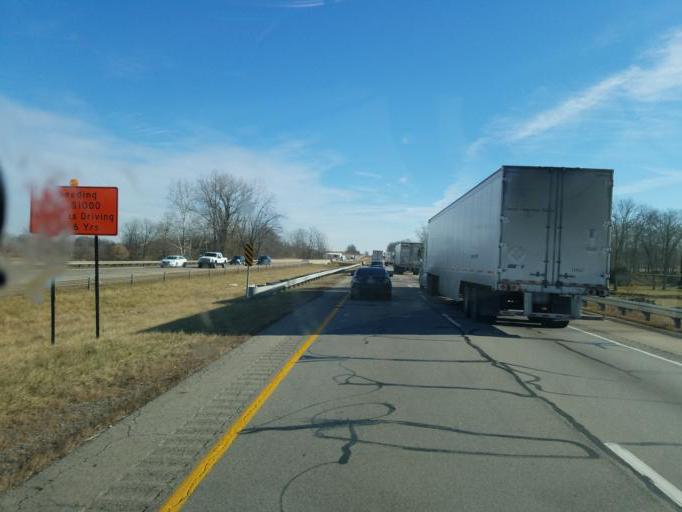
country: US
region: Indiana
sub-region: Wayne County
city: Cambridge City
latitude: 39.8530
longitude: -85.1704
